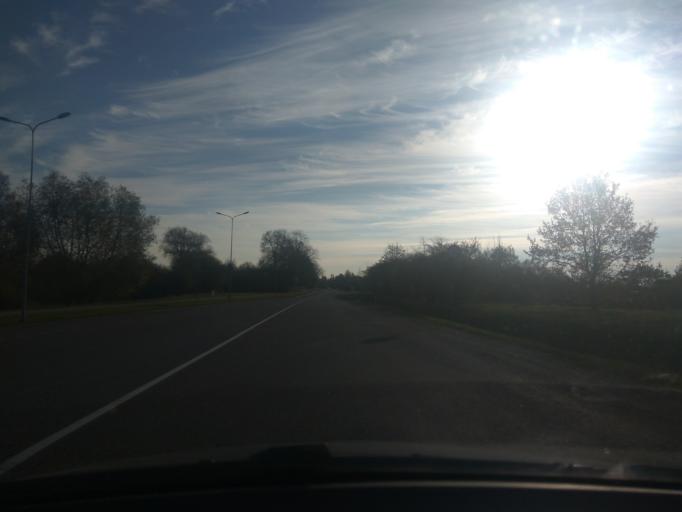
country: LV
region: Ventspils
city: Ventspils
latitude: 57.3674
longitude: 21.5644
